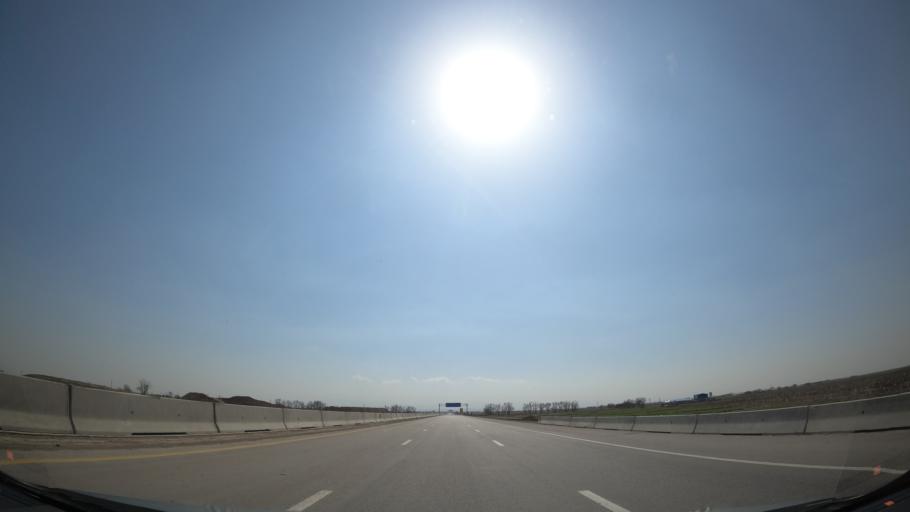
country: IR
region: Qazvin
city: Abyek
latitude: 35.9822
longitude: 50.4616
